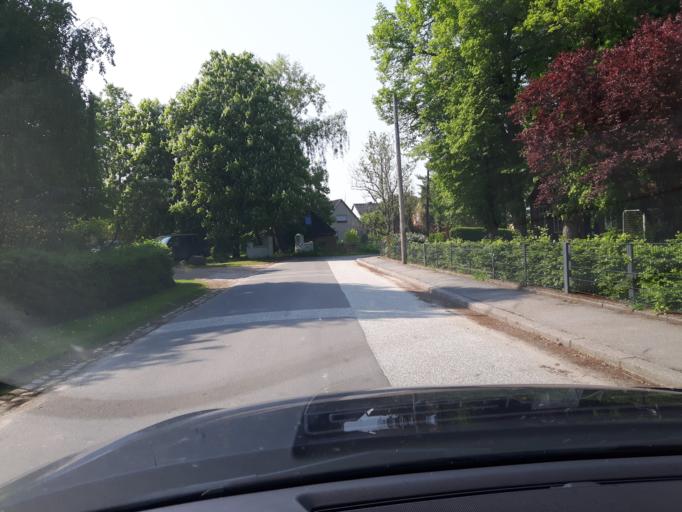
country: DE
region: Schleswig-Holstein
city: Travemuende
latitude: 53.9387
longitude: 10.8401
